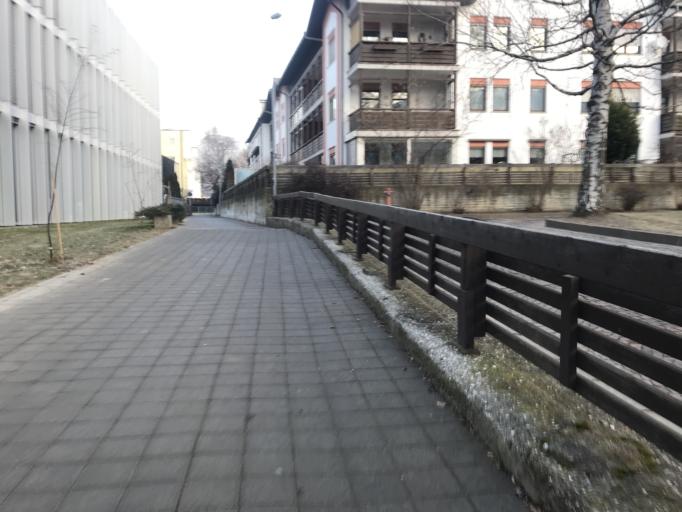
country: IT
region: Trentino-Alto Adige
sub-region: Bolzano
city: Bressanone
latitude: 46.7221
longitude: 11.6519
